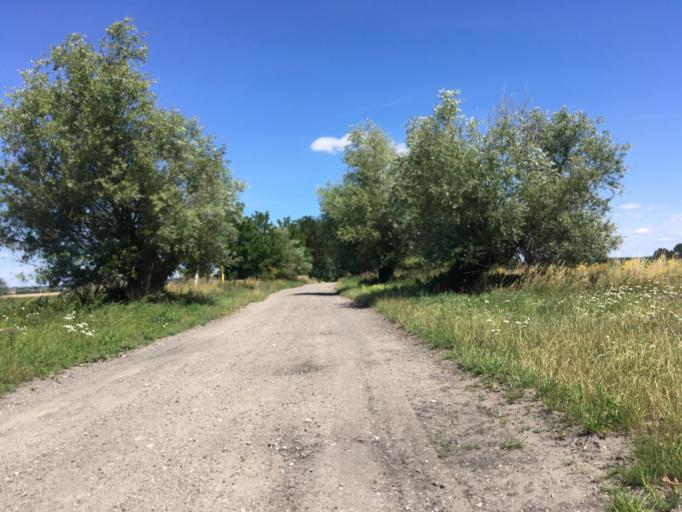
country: DE
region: Brandenburg
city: Grunow
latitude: 53.3332
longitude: 13.9953
